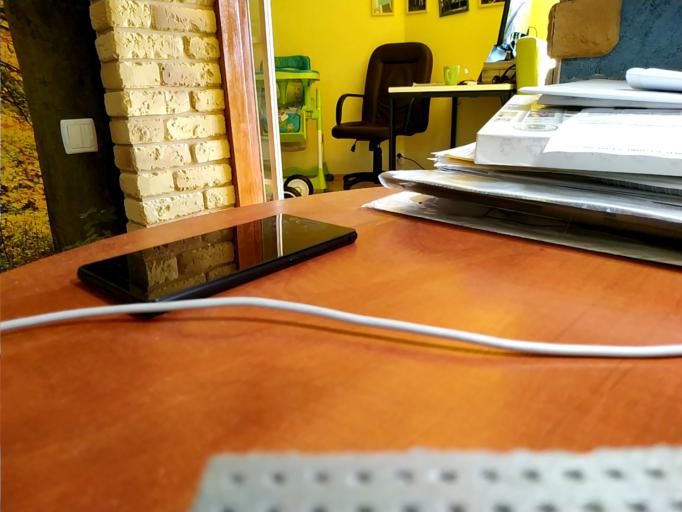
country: RU
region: Tverskaya
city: Kalashnikovo
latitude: 57.3674
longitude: 35.4332
